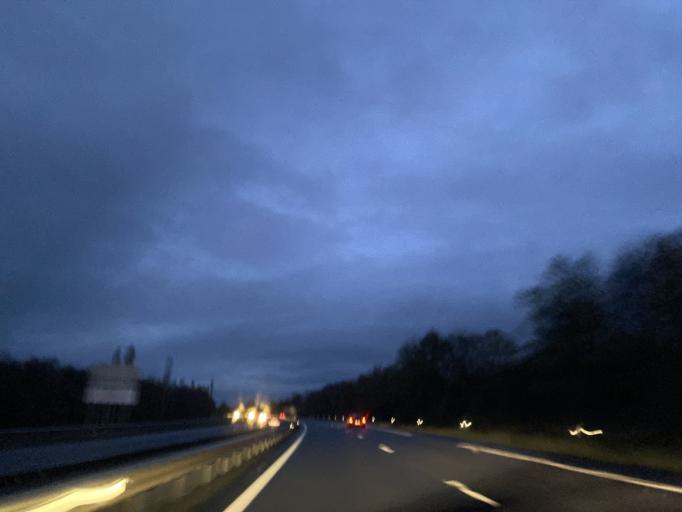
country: FR
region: Auvergne
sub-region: Departement de l'Allier
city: Montmarault
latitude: 46.3239
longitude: 2.9260
